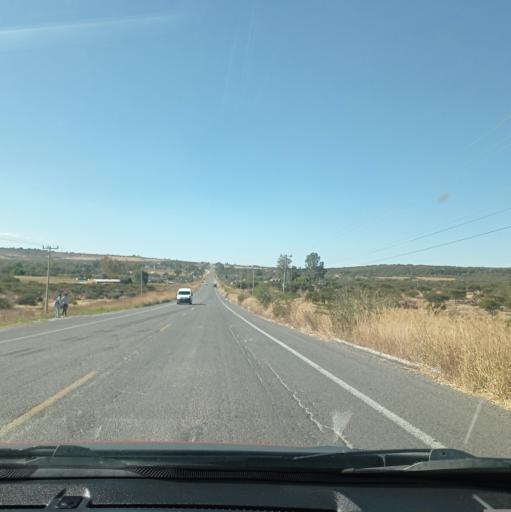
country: MX
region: Jalisco
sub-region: San Julian
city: Colonia Veintitres de Mayo
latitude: 21.0062
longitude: -102.2864
